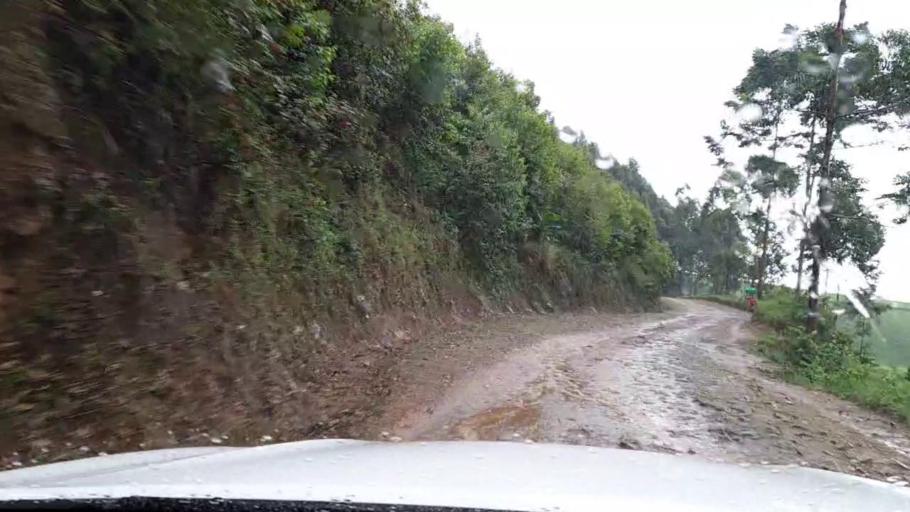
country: RW
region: Western Province
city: Cyangugu
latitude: -2.4604
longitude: 29.0367
